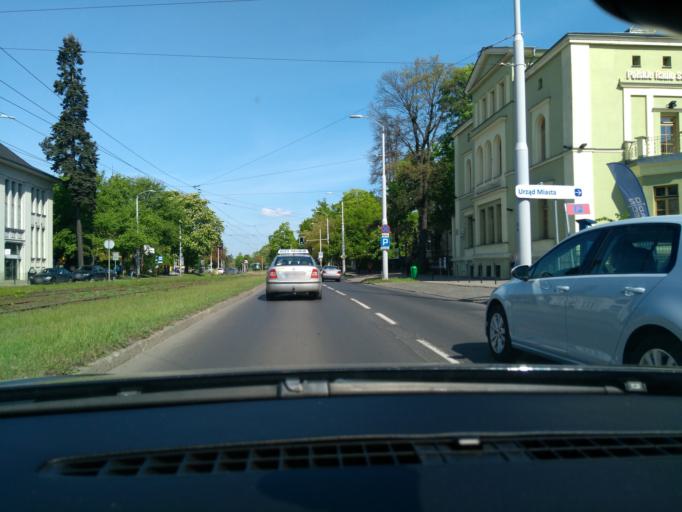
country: PL
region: West Pomeranian Voivodeship
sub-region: Szczecin
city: Szczecin
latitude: 53.4351
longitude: 14.5390
